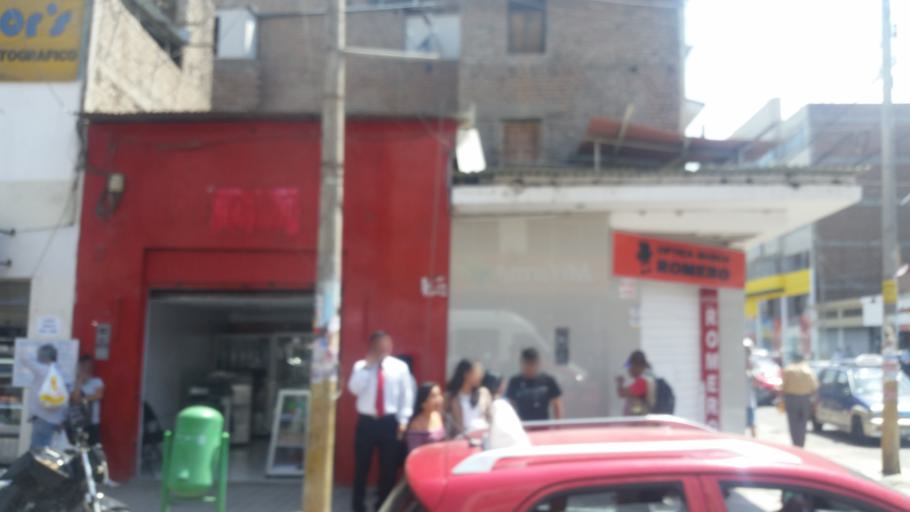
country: PE
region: Lambayeque
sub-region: Provincia de Chiclayo
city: Chiclayo
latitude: -6.7708
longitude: -79.8421
